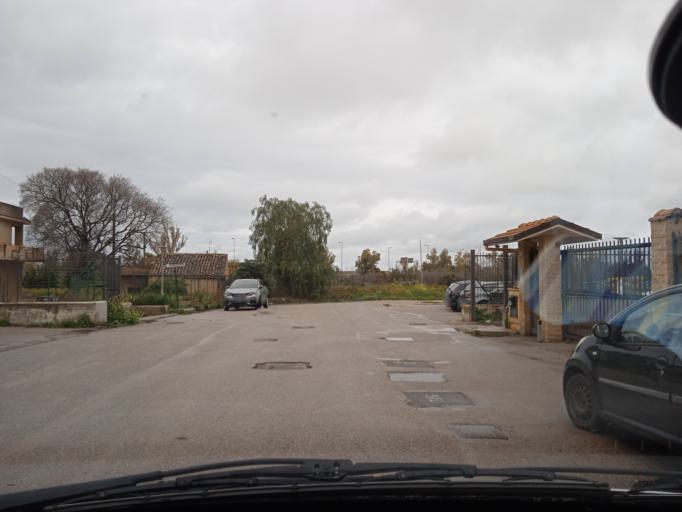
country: IT
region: Sicily
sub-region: Palermo
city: Villabate
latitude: 38.0815
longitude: 13.4451
